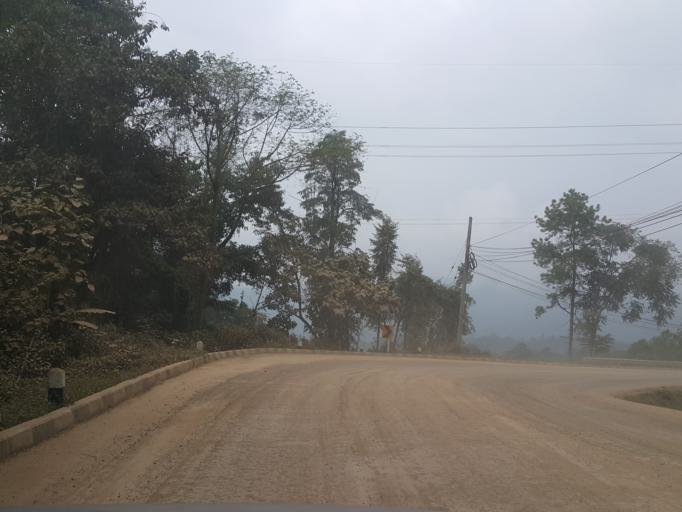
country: TH
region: Mae Hong Son
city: Mae Hi
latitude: 19.2709
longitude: 98.5450
